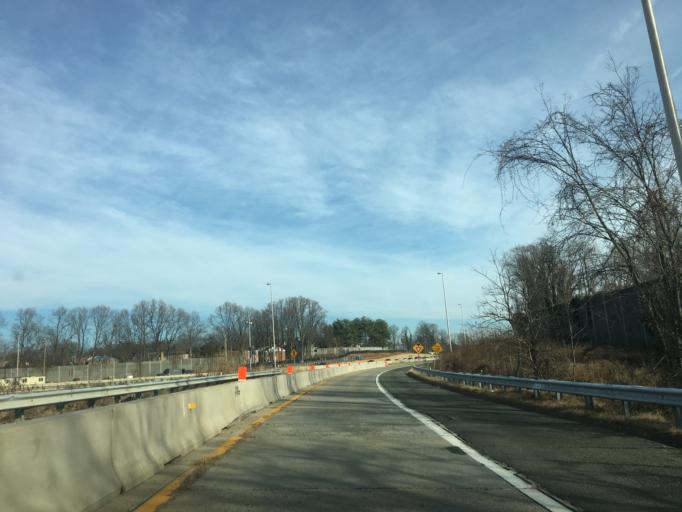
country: US
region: Virginia
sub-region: Fairfax County
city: Oakton
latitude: 38.8686
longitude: -77.3056
